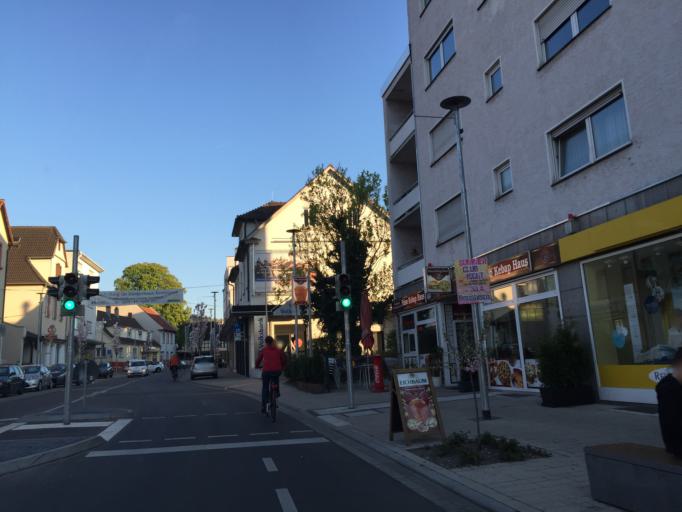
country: DE
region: Hesse
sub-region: Regierungsbezirk Darmstadt
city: Bensheim
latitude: 49.7028
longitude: 8.6195
